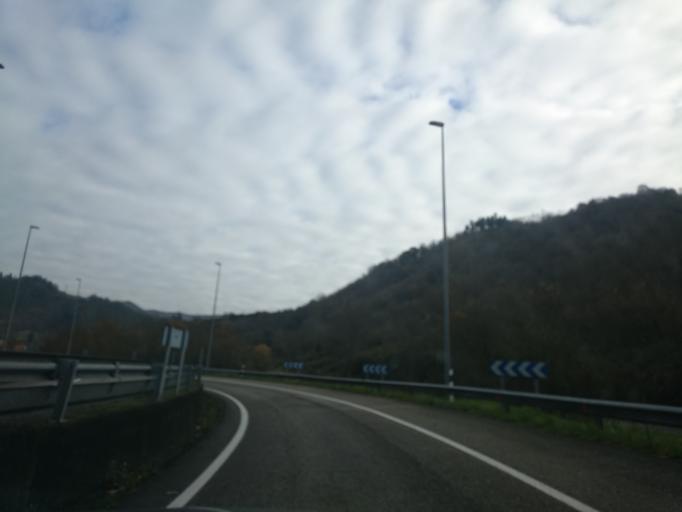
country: ES
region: Asturias
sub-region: Province of Asturias
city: Castandiello
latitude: 43.2968
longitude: -5.8333
